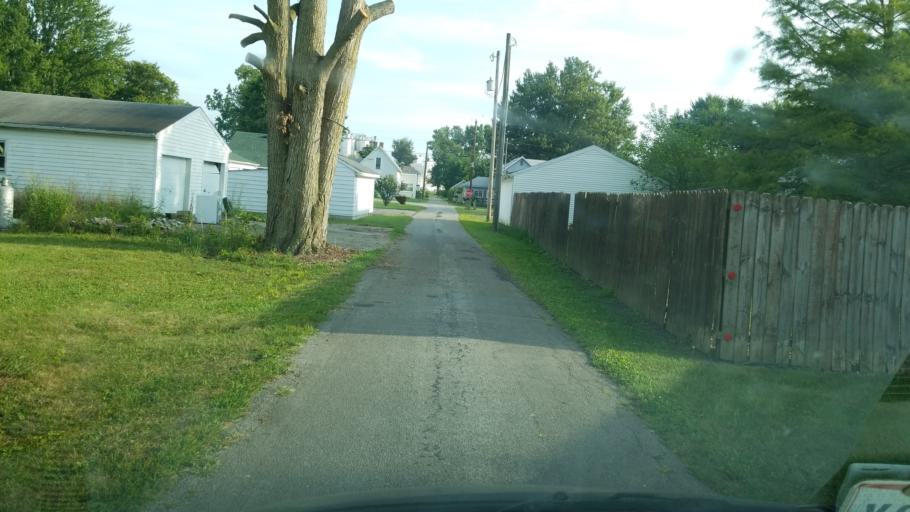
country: US
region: Ohio
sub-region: Crawford County
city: Galion
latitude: 40.6674
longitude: -82.9087
